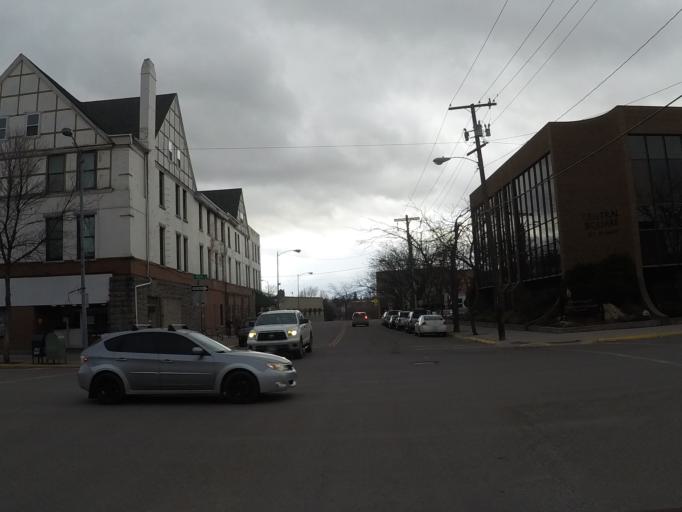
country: US
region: Montana
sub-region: Missoula County
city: Missoula
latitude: 46.8718
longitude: -113.9962
